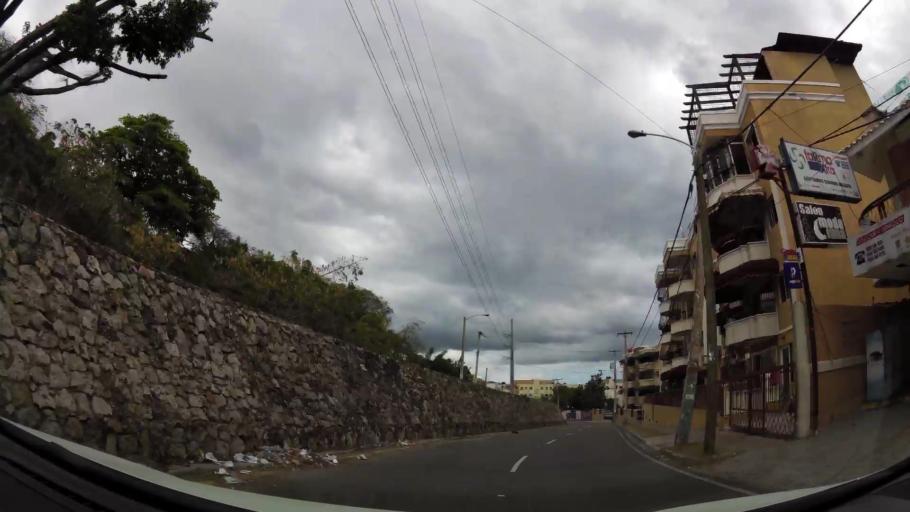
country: DO
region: Nacional
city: Bella Vista
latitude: 18.4411
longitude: -69.9573
